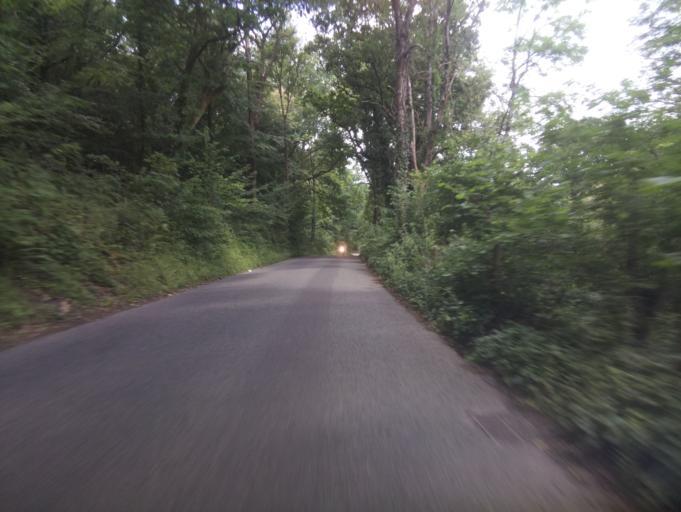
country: GB
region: England
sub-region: Gloucestershire
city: Bream
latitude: 51.7414
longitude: -2.5571
